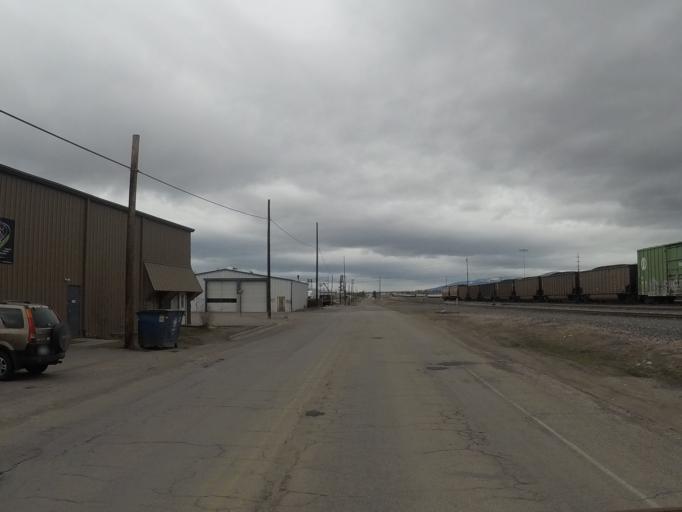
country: US
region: Montana
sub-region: Missoula County
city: Missoula
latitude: 46.8915
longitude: -114.0246
